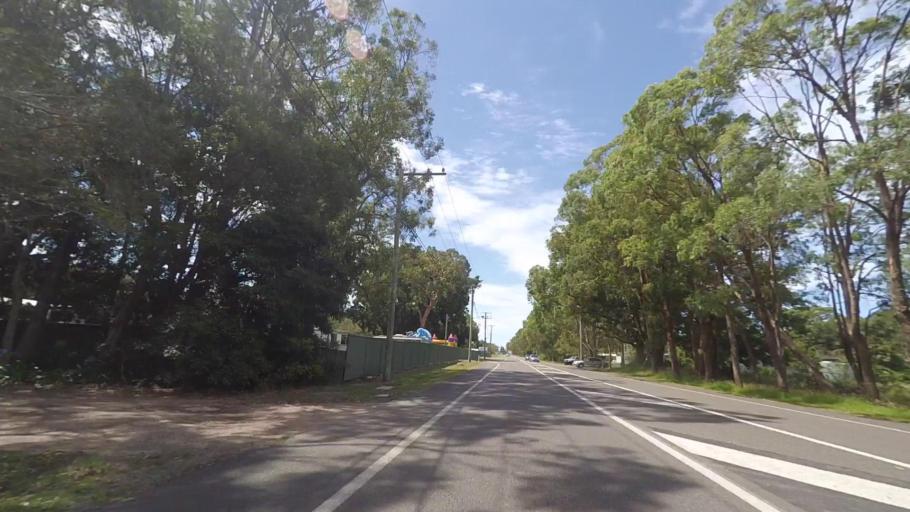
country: AU
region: New South Wales
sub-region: Port Stephens Shire
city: Anna Bay
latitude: -32.7579
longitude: 152.0677
